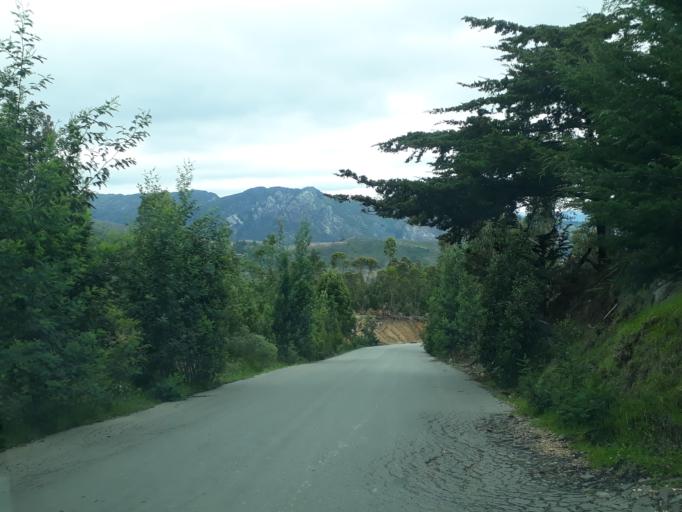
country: CO
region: Cundinamarca
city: Cucunuba
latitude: 5.2196
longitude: -73.7826
